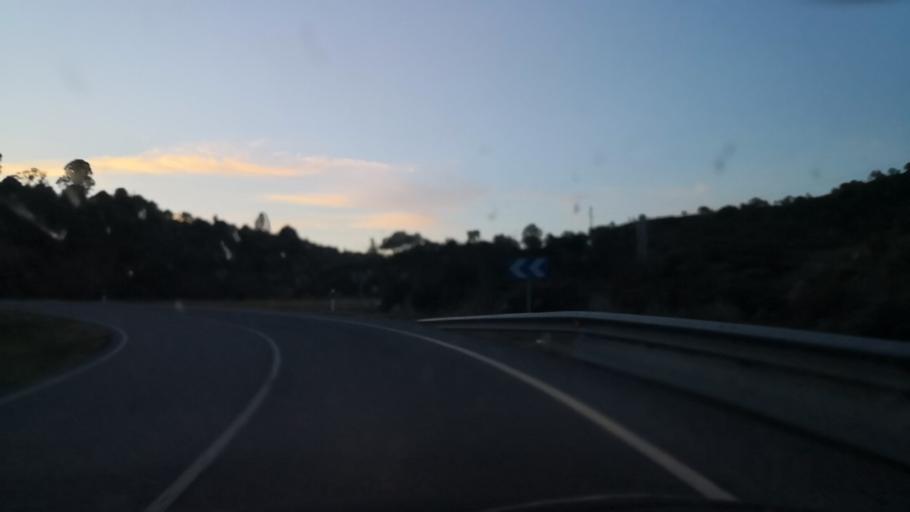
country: ES
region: Extremadura
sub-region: Provincia de Caceres
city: Alcantara
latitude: 39.7291
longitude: -6.8935
